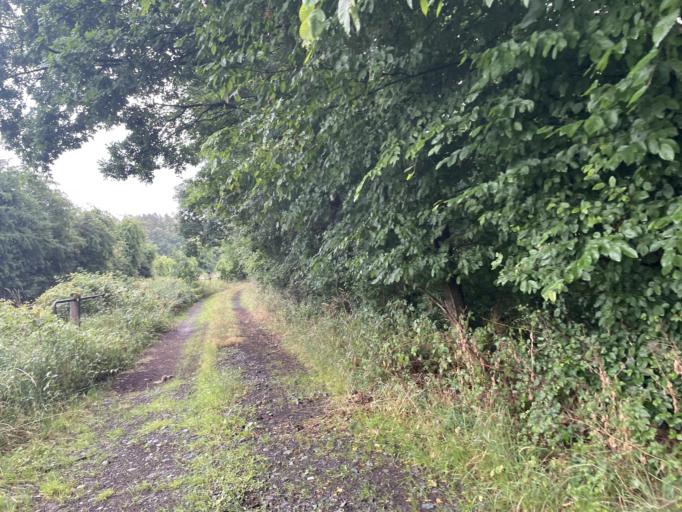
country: DE
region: Bavaria
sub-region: Upper Franconia
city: Neunkirchen am Main
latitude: 49.9345
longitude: 11.6357
